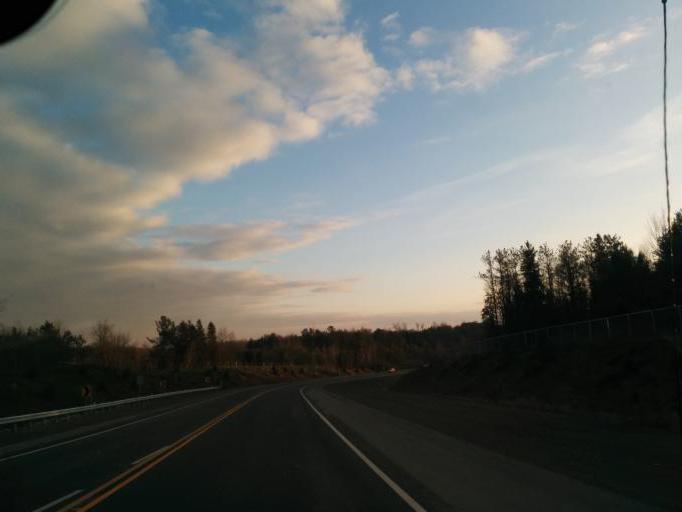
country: CA
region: Ontario
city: Brampton
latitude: 43.8876
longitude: -79.7721
